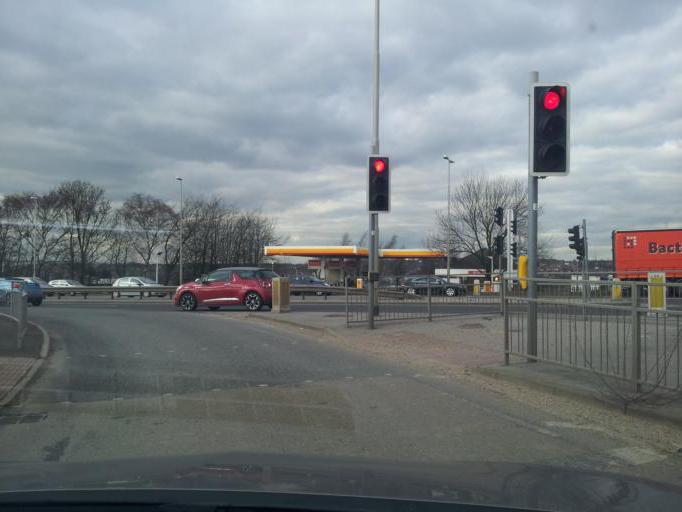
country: GB
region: England
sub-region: Derbyshire
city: Pinxton
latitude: 53.1113
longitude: -1.2967
